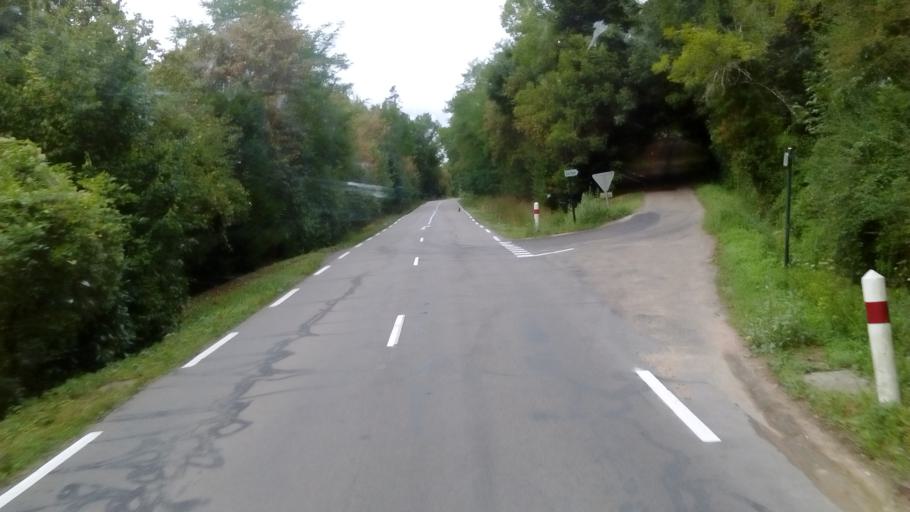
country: FR
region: Bourgogne
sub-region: Departement de Saone-et-Loire
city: Saint-Yan
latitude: 46.4341
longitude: 4.0211
